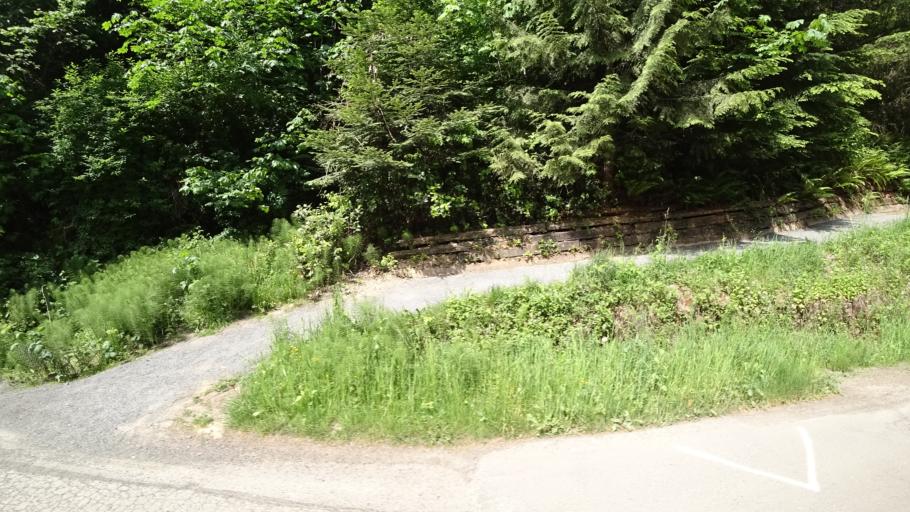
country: US
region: Oregon
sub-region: Multnomah County
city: Portland
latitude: 45.5188
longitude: -122.7181
